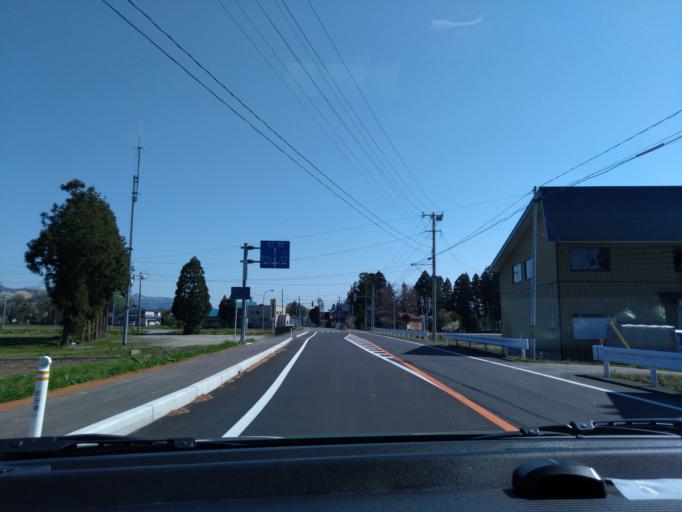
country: JP
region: Akita
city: Kakunodatemachi
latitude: 39.5334
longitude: 140.5852
